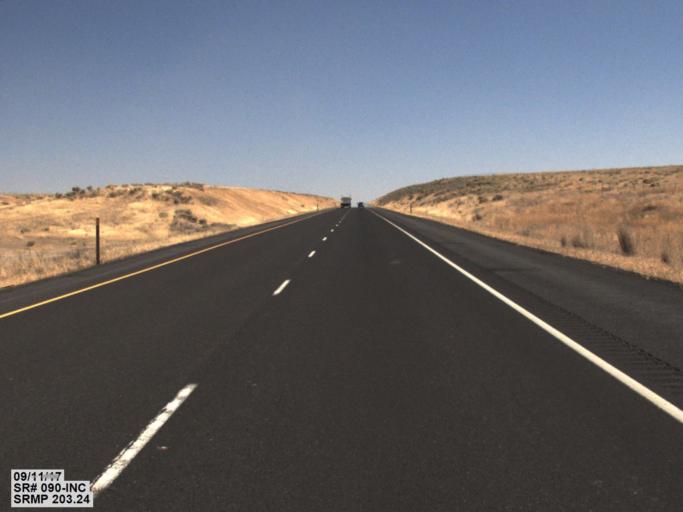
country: US
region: Washington
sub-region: Grant County
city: Warden
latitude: 47.0860
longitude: -118.7411
